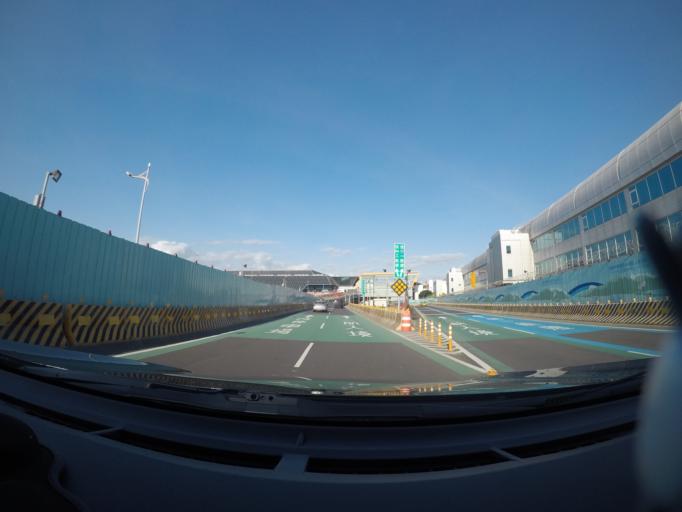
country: TW
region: Taiwan
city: Taoyuan City
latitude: 25.0742
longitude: 121.2305
